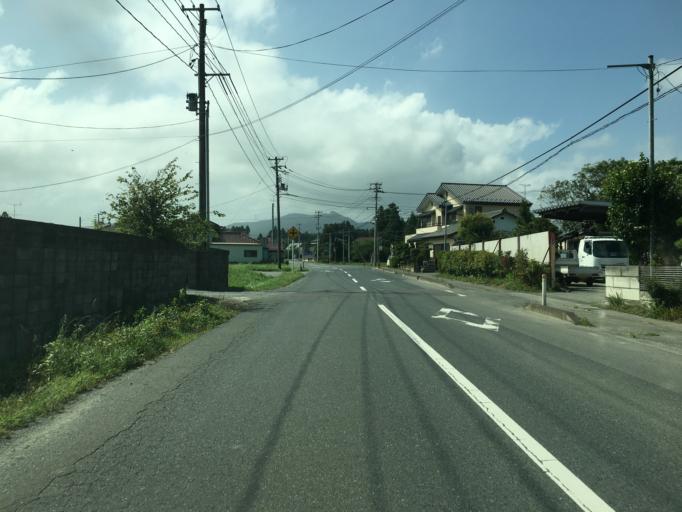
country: JP
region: Miyagi
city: Marumori
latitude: 37.8374
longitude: 140.9033
